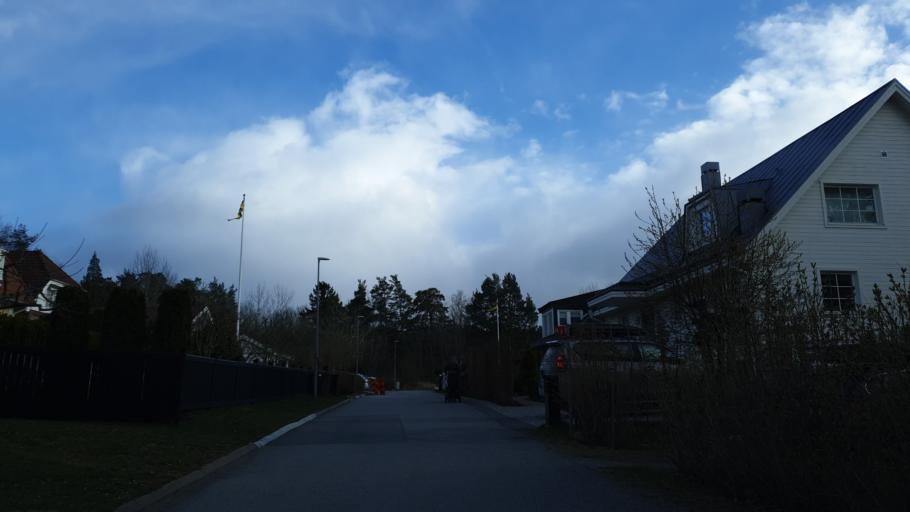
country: SE
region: Stockholm
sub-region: Lidingo
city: Lidingoe
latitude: 59.3900
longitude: 18.1206
